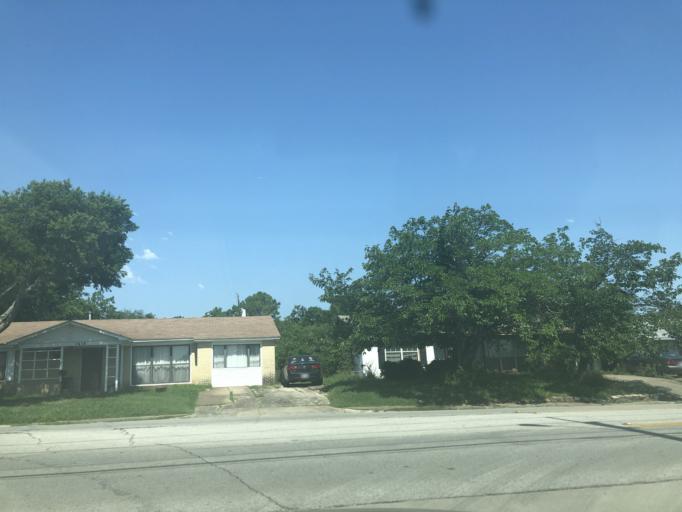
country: US
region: Texas
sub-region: Dallas County
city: Grand Prairie
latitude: 32.7235
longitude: -97.0070
